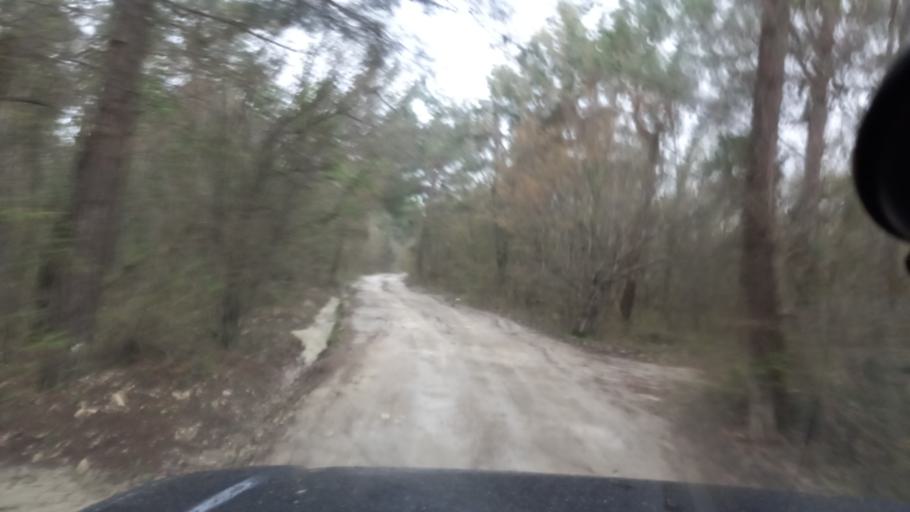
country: RU
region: Krasnodarskiy
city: Dzhubga
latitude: 44.3187
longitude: 38.6879
